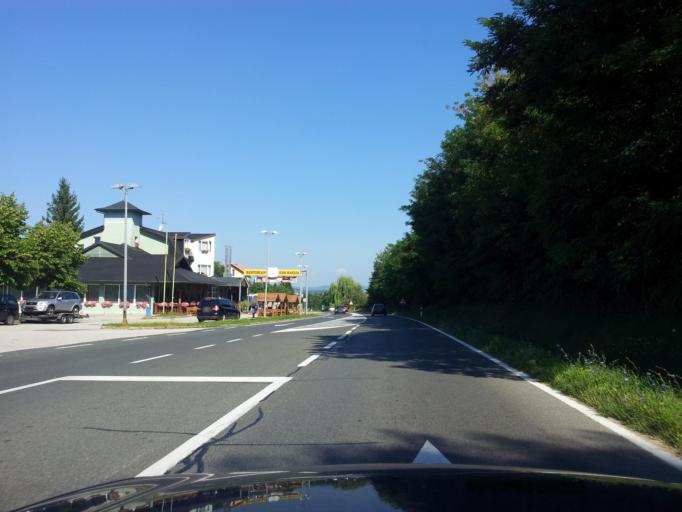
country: HR
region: Karlovacka
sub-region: Grad Karlovac
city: Karlovac
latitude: 45.4446
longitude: 15.5840
